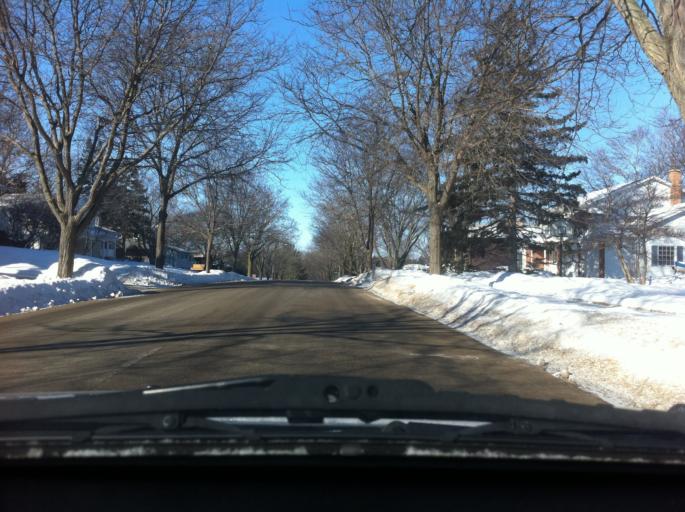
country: US
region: Wisconsin
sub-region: Dane County
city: Shorewood Hills
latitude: 43.0633
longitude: -89.4815
